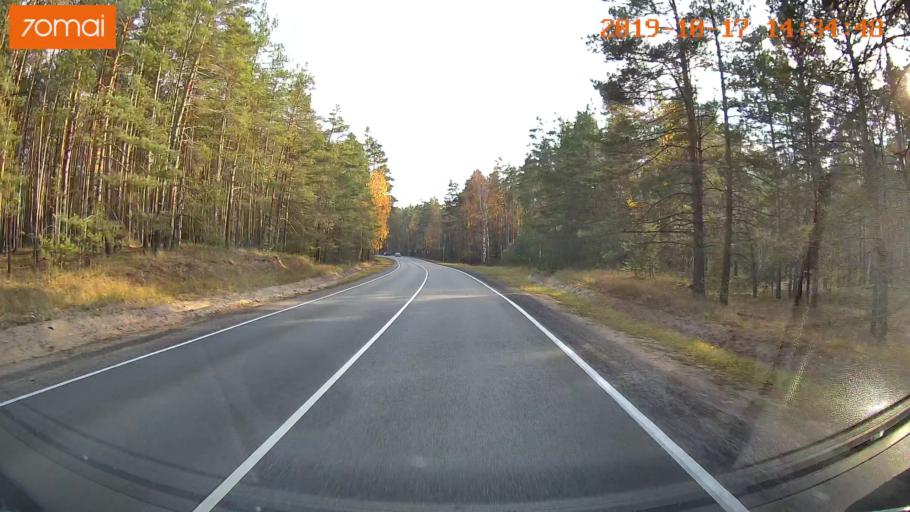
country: RU
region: Rjazan
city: Solotcha
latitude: 54.9073
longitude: 39.9994
